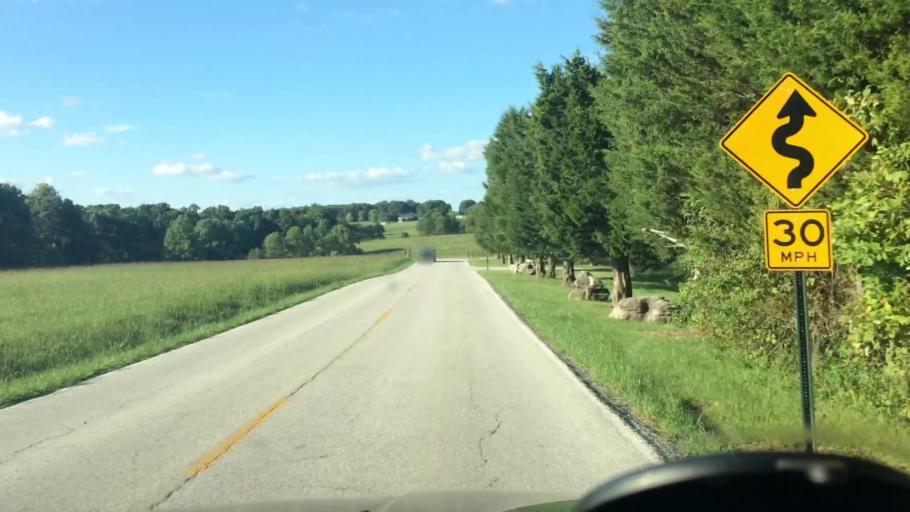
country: US
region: Missouri
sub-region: Greene County
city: Strafford
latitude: 37.2725
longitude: -93.0813
